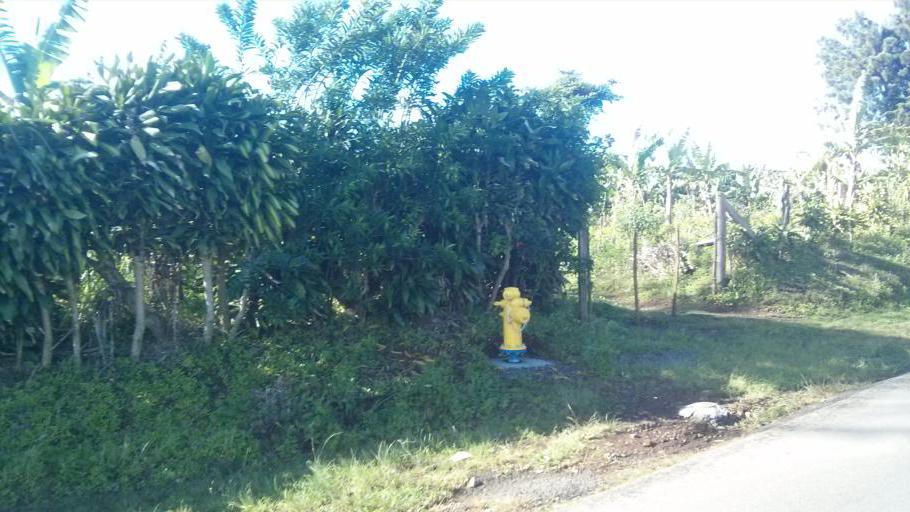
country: CR
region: Heredia
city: Angeles
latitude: 10.0142
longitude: -84.0511
